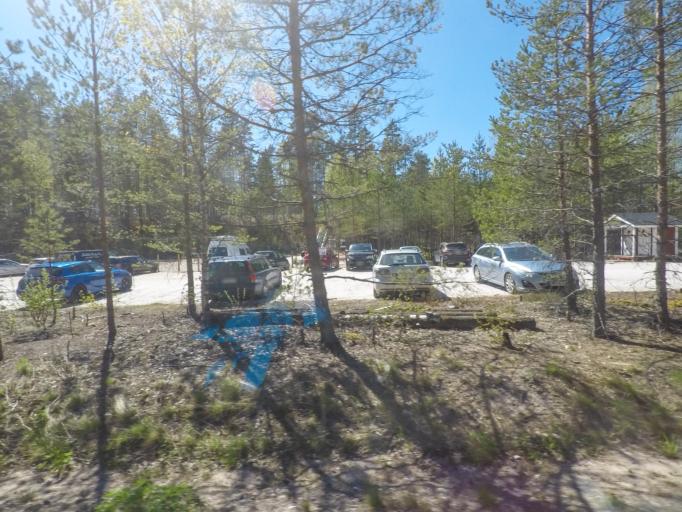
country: FI
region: Uusimaa
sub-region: Helsinki
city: Sammatti
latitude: 60.3318
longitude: 23.8120
